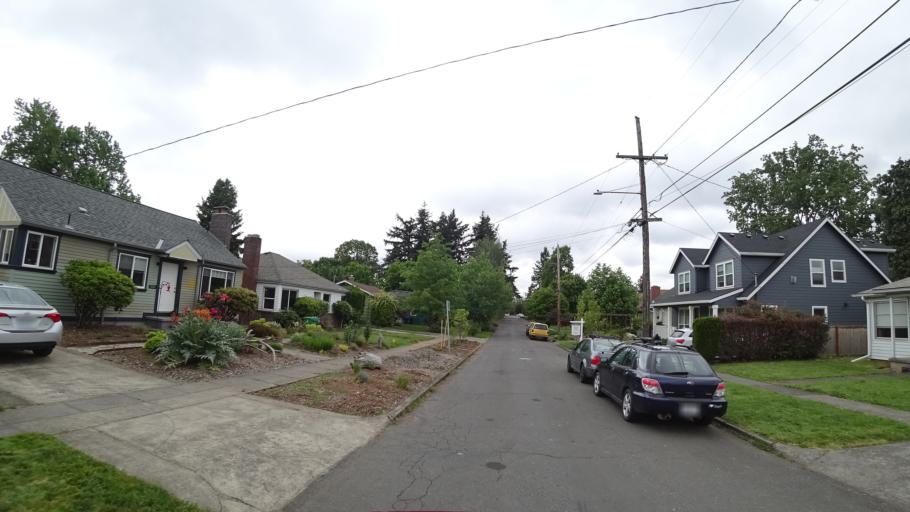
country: US
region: Oregon
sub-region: Multnomah County
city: Lents
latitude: 45.4912
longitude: -122.6149
